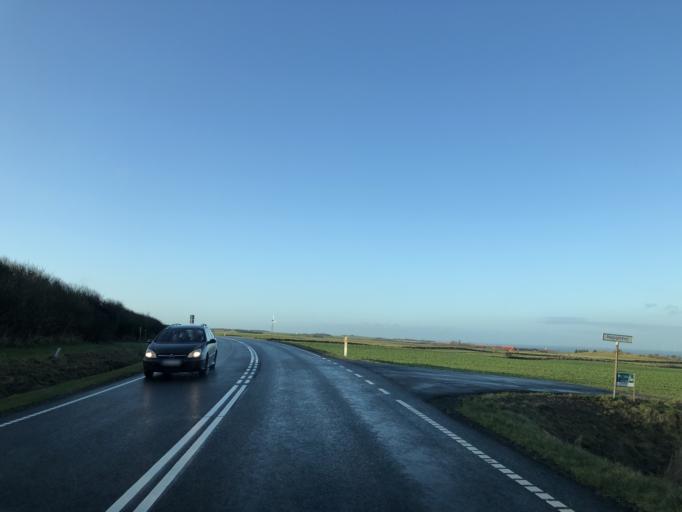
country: DK
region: Central Jutland
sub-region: Lemvig Kommune
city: Lemvig
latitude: 56.5603
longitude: 8.4236
